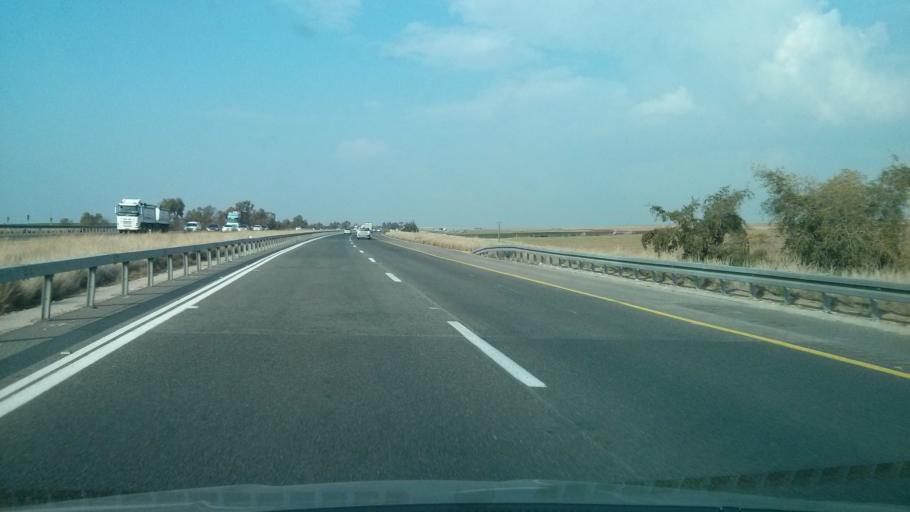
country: IL
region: Central District
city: Gedera
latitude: 31.7496
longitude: 34.8237
